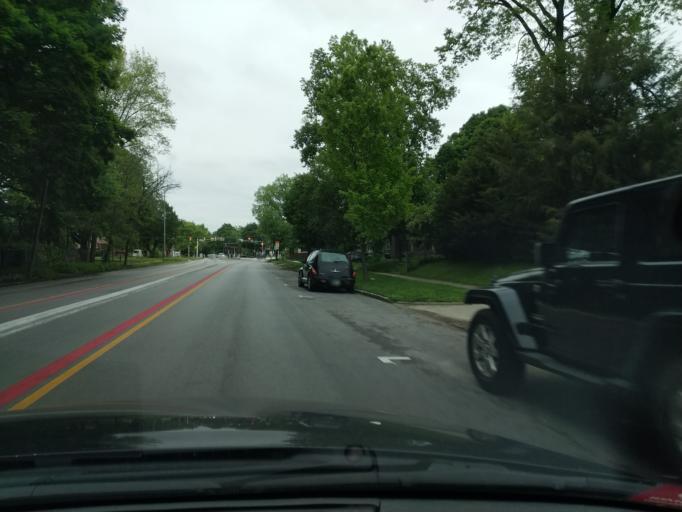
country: US
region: Indiana
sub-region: Marion County
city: Broad Ripple
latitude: 39.8382
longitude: -86.1452
